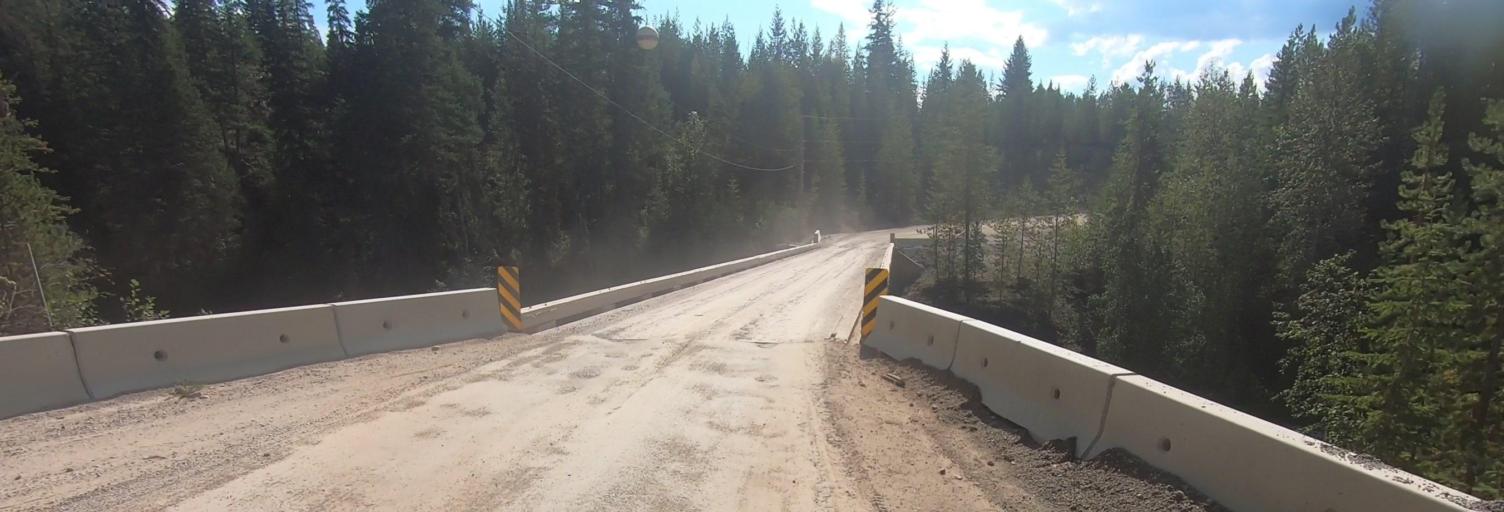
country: CA
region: British Columbia
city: Golden
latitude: 51.4994
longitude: -117.1762
